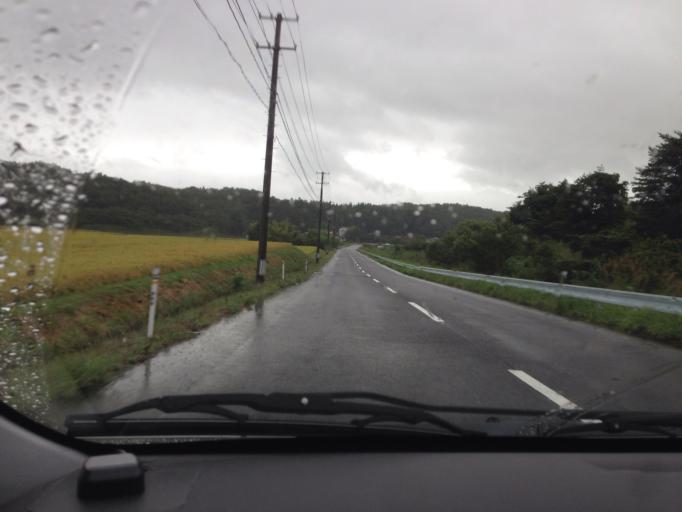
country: JP
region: Fukushima
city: Koriyama
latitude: 37.4519
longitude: 140.2789
